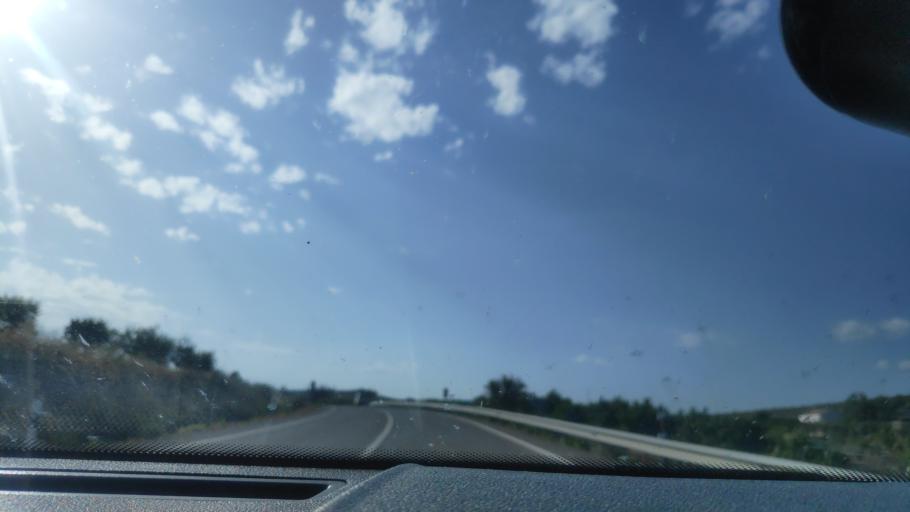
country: ES
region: Andalusia
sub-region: Provincia de Jaen
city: Frailes
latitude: 37.4503
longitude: -3.8688
